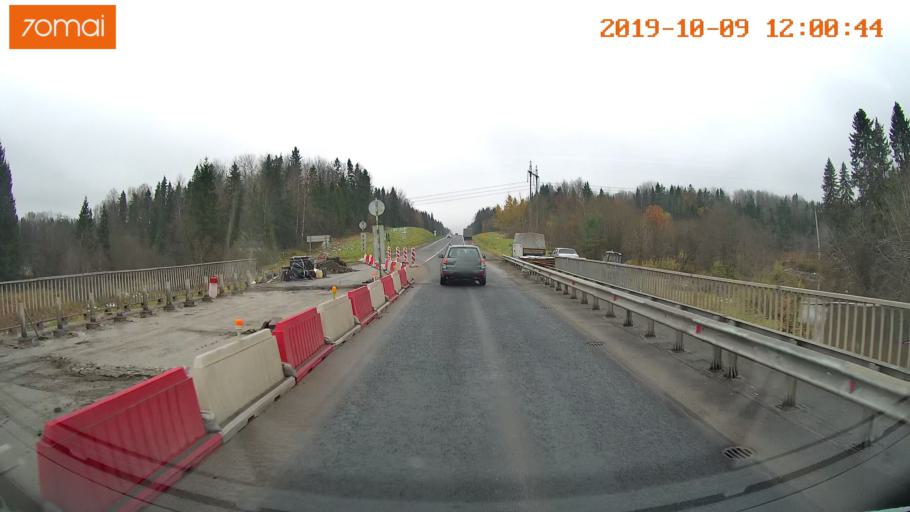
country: RU
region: Vologda
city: Gryazovets
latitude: 58.6947
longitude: 40.3005
